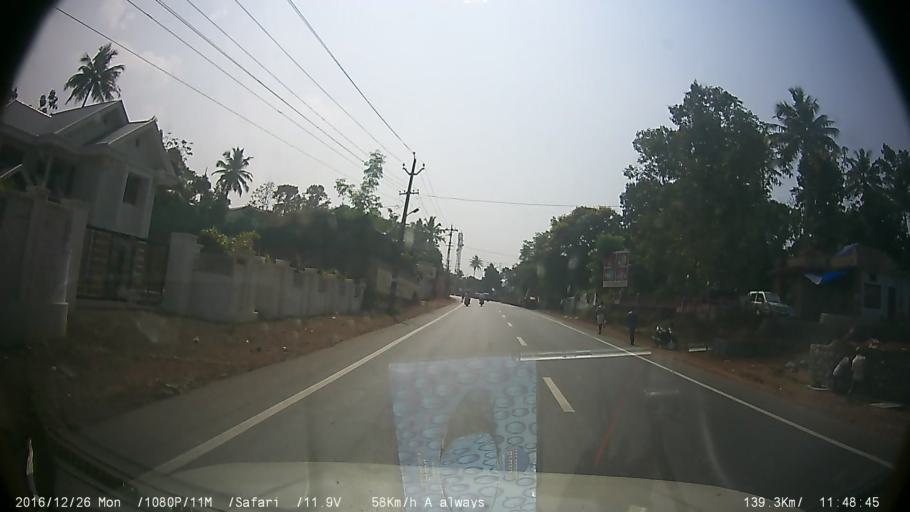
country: IN
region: Kerala
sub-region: Kottayam
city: Changanacheri
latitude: 9.4897
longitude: 76.5248
